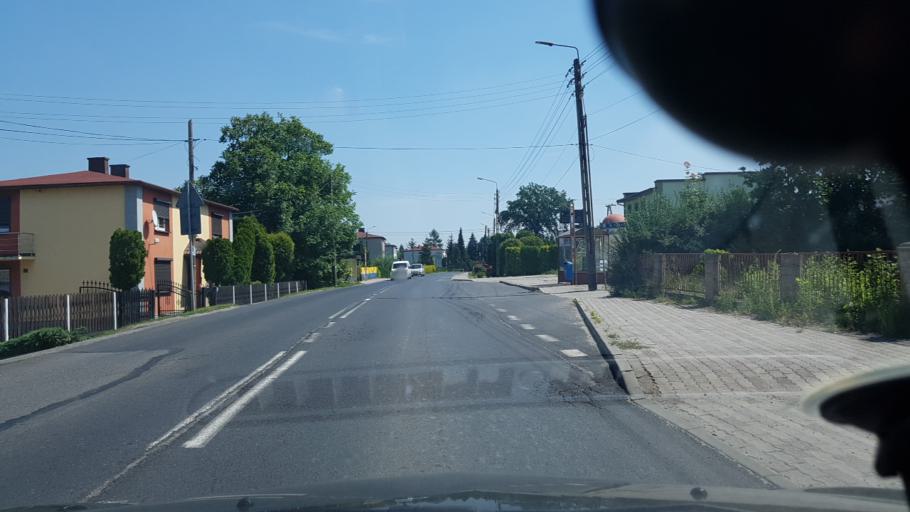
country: PL
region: Silesian Voivodeship
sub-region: Powiat wodzislawski
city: Marklowice
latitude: 50.0177
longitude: 18.5300
